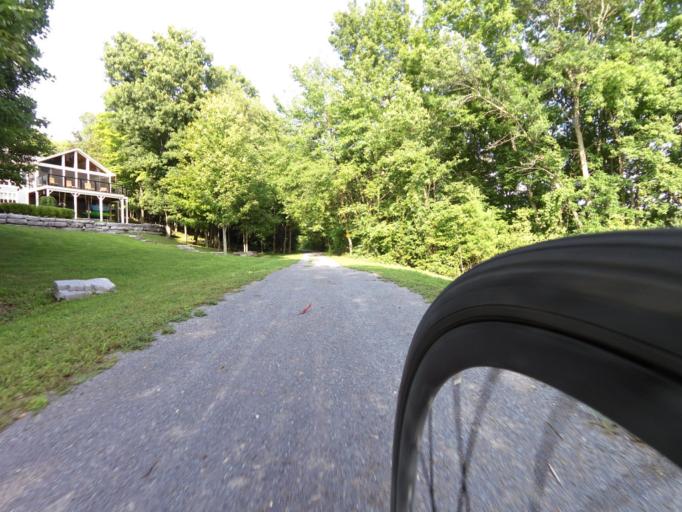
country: CA
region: Ontario
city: Kingston
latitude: 44.4310
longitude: -76.5447
